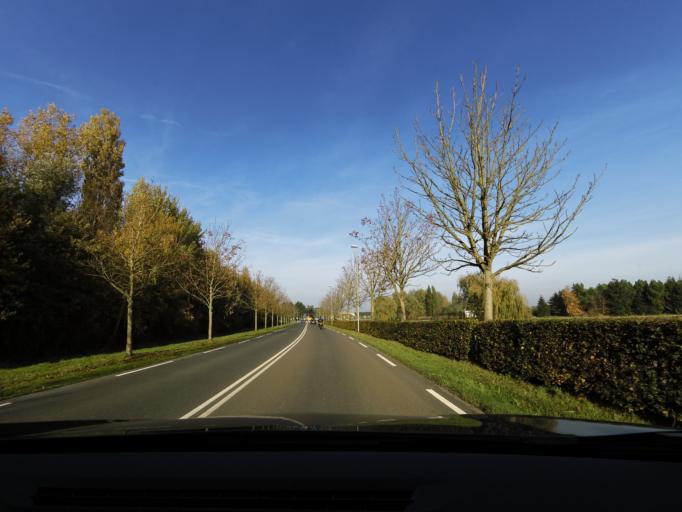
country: NL
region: South Holland
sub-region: Gemeente Zwijndrecht
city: Heerjansdam
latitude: 51.8460
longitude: 4.5572
